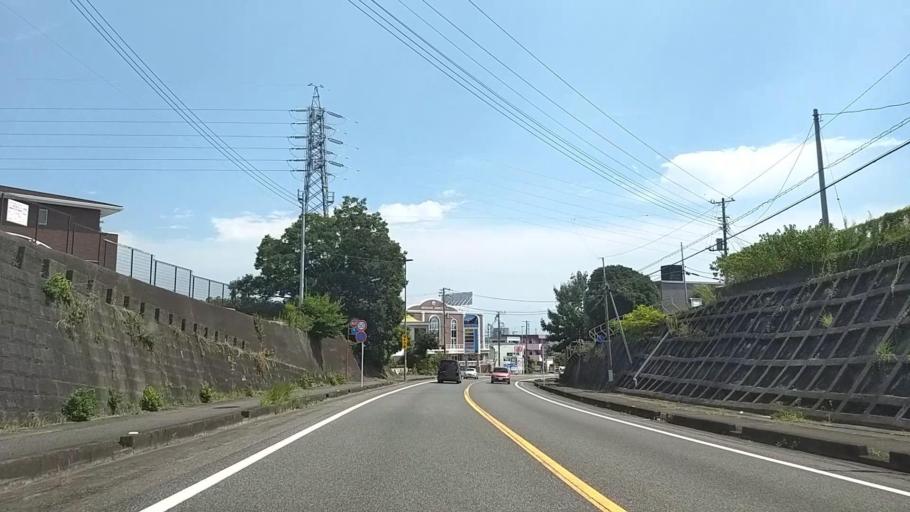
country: JP
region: Shizuoka
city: Fuji
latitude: 35.1711
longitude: 138.6783
